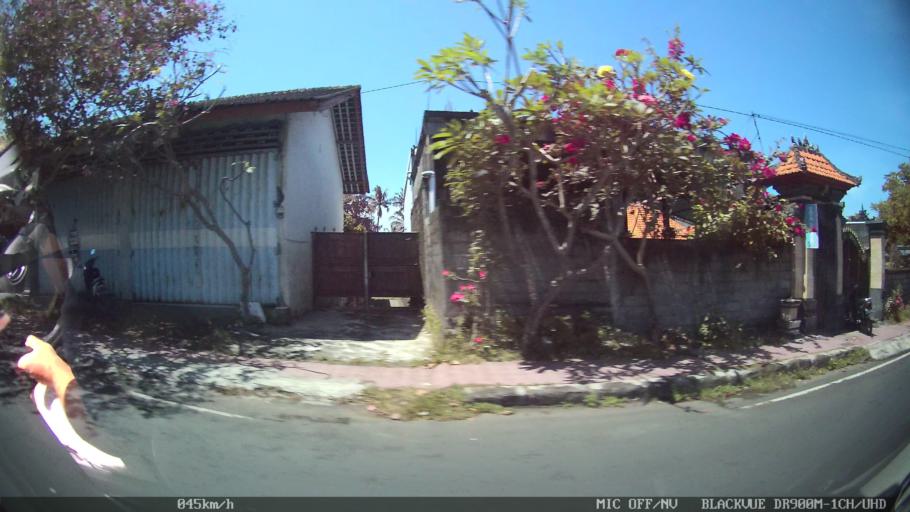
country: ID
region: Bali
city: Klungkung
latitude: -8.5708
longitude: 115.3483
